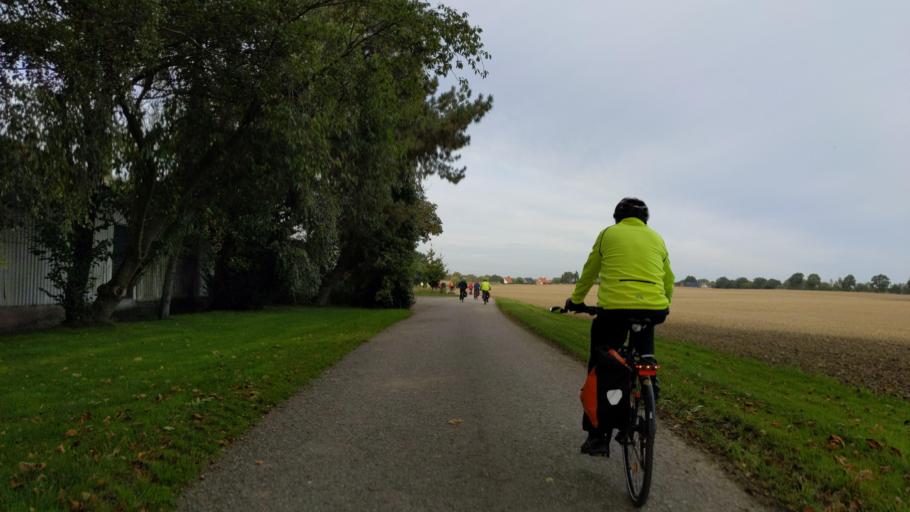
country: DE
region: Schleswig-Holstein
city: Rehhorst
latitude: 53.8855
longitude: 10.4861
